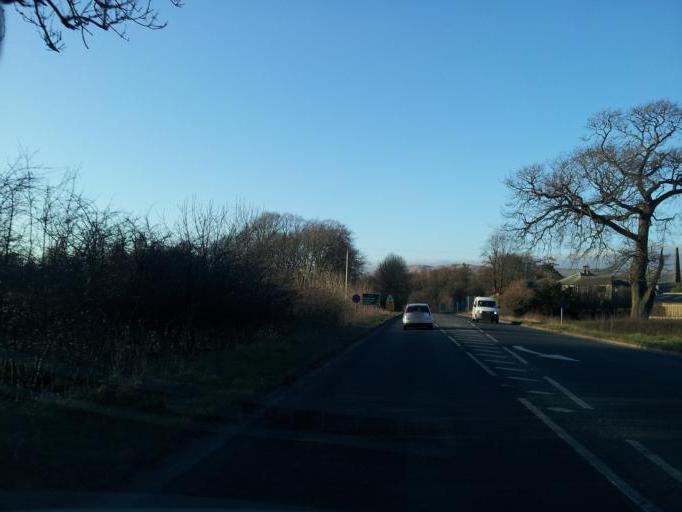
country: GB
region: England
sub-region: Cumbria
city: Kendal
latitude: 54.3470
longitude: -2.7760
